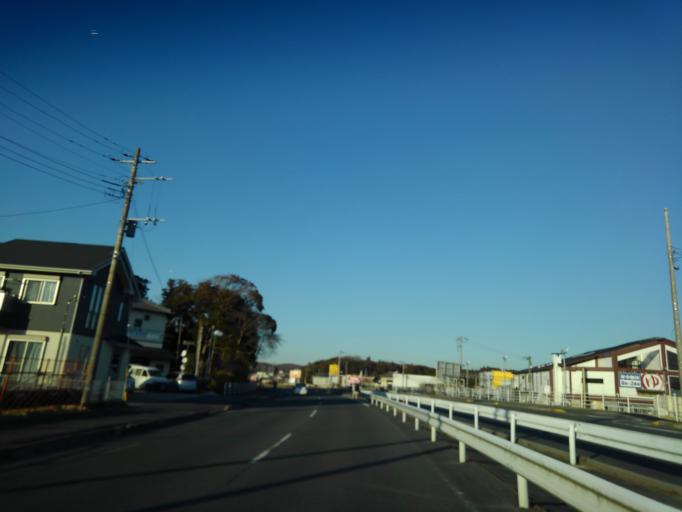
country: JP
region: Chiba
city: Kimitsu
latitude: 35.3138
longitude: 139.9268
